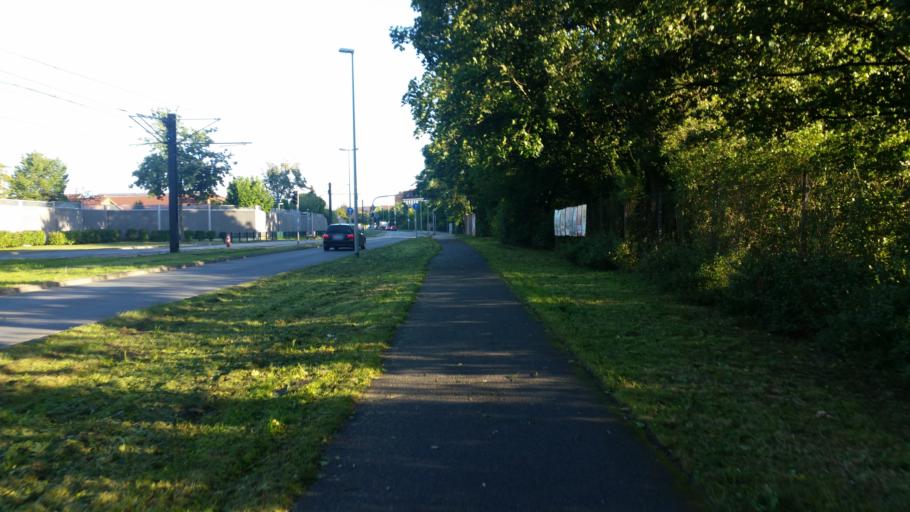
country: DE
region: Lower Saxony
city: Isernhagen Farster Bauerschaft
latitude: 52.4024
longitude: 9.8261
